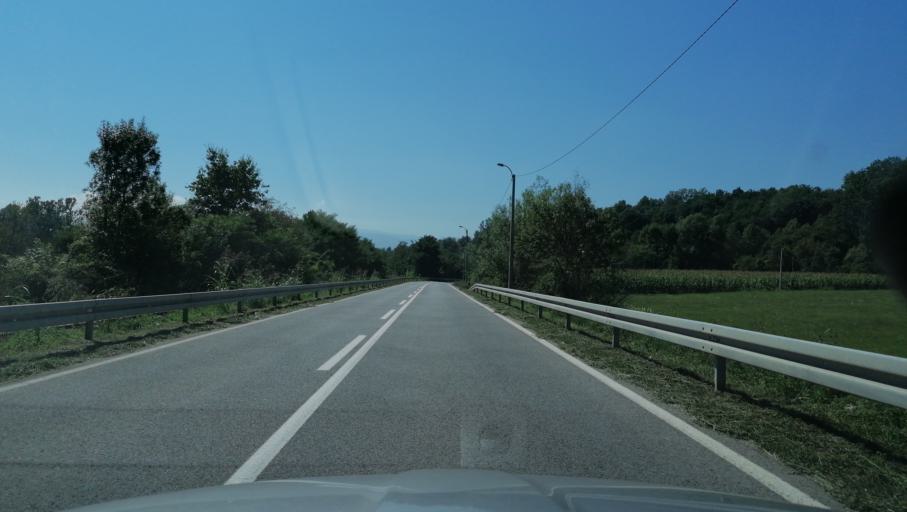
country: RS
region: Central Serbia
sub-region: Raski Okrug
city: Kraljevo
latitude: 43.7222
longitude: 20.7975
